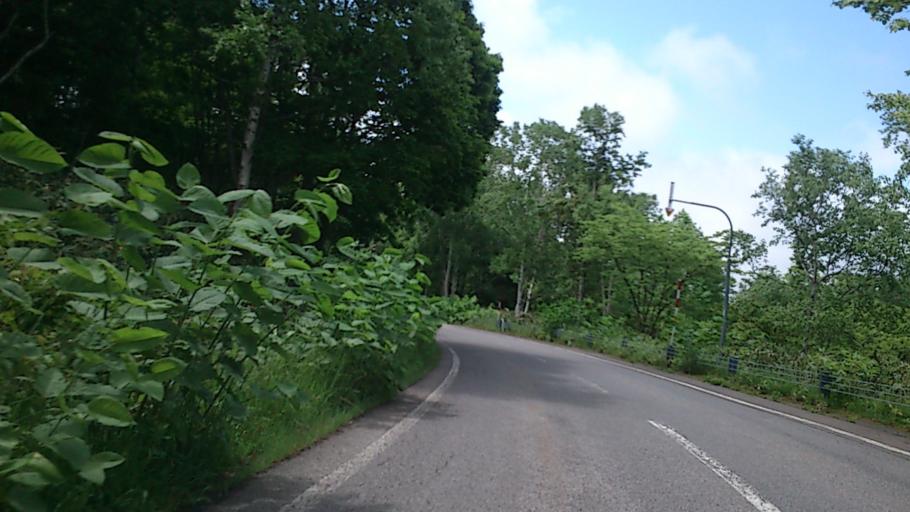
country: JP
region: Hokkaido
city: Niseko Town
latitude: 42.8362
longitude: 140.5422
